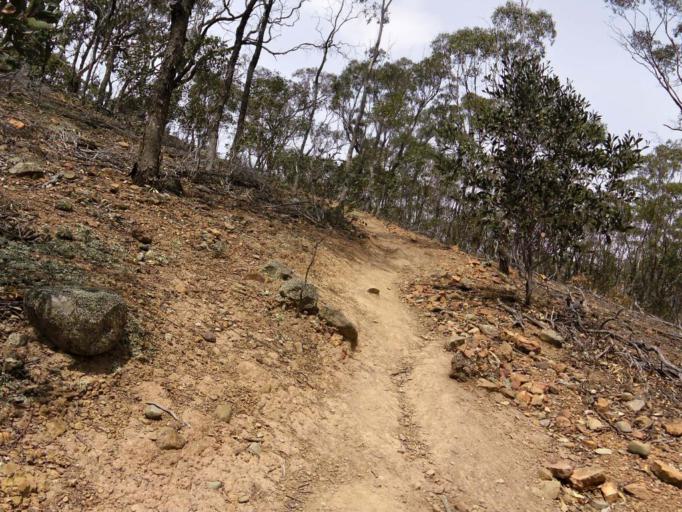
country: AU
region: Victoria
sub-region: Moorabool
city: Bacchus Marsh
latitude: -37.6667
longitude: 144.3655
